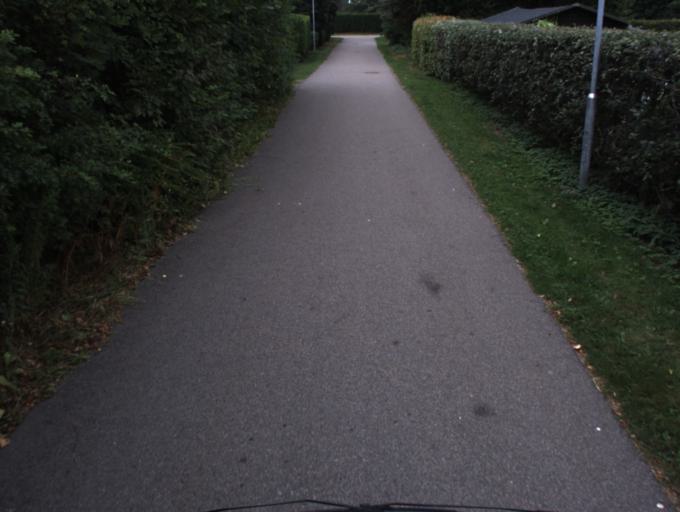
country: SE
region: Skane
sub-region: Helsingborg
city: Morarp
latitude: 56.0549
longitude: 12.8759
